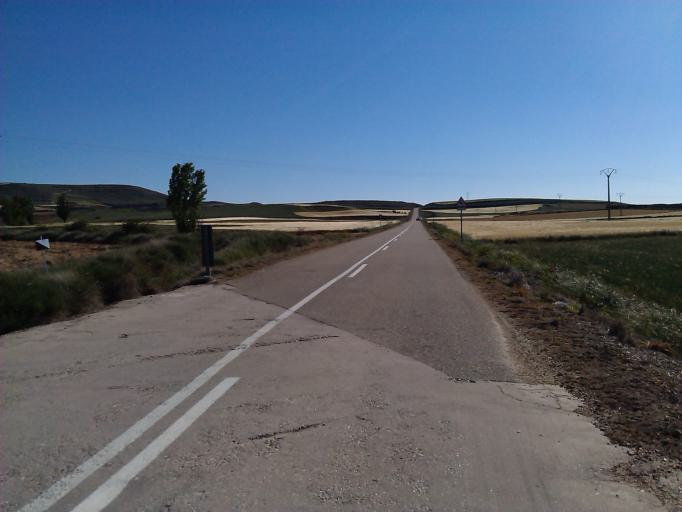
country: ES
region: Castille and Leon
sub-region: Provincia de Burgos
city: Pedrosa del Principe
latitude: 42.3089
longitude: -4.1757
